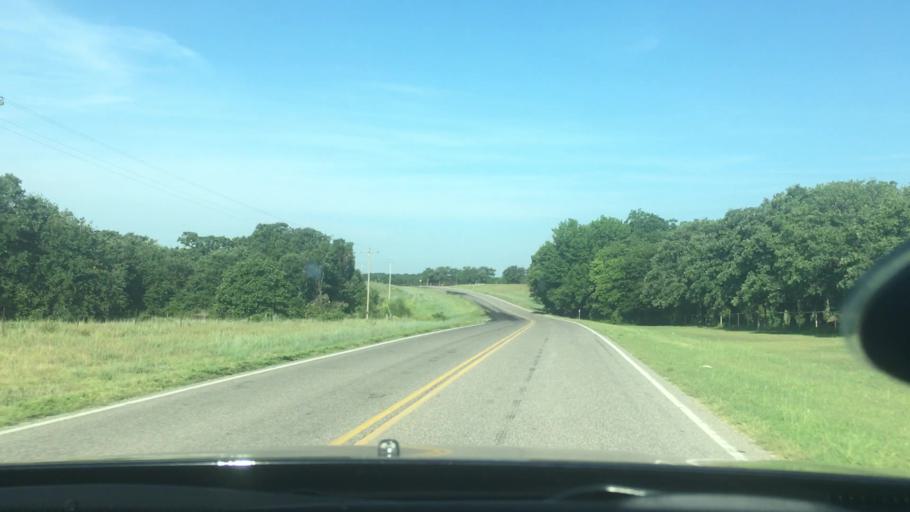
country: US
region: Oklahoma
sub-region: Garvin County
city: Pauls Valley
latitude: 34.6521
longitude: -97.3478
